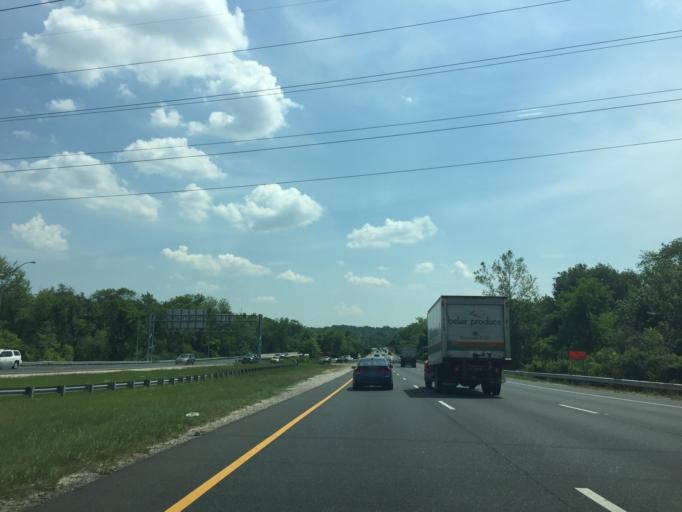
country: US
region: Maryland
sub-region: Baltimore County
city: Baltimore Highlands
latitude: 39.2318
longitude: -76.6501
